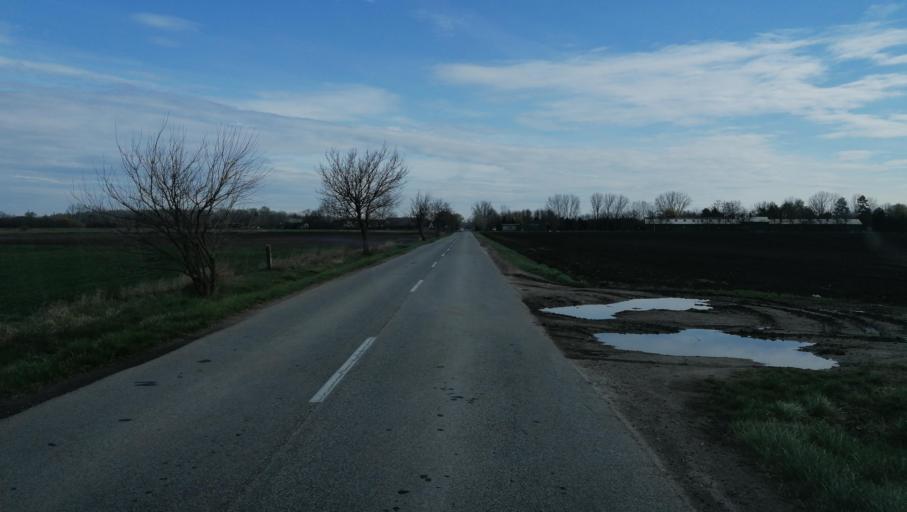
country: HU
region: Pest
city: Rackeve
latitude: 47.1150
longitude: 18.9420
